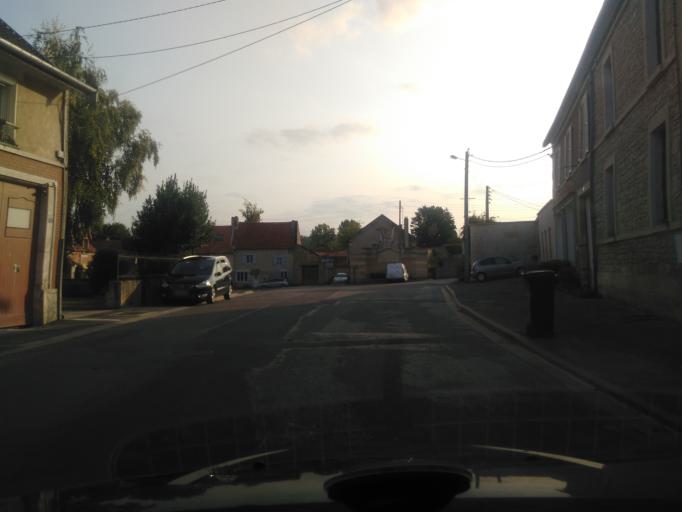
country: FR
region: Champagne-Ardenne
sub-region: Departement de la Marne
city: Fismes
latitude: 49.2686
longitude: 3.6970
